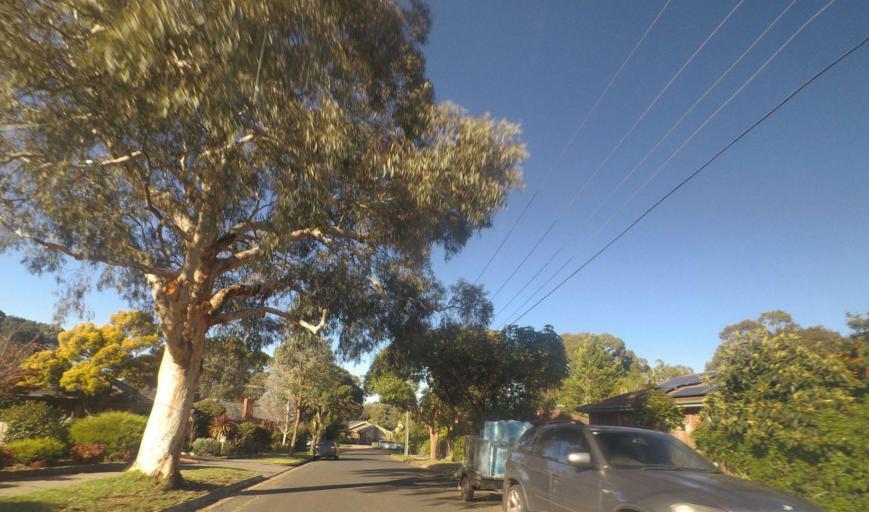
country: AU
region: Victoria
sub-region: Whitehorse
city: Blackburn North
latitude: -37.8124
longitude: 145.1464
